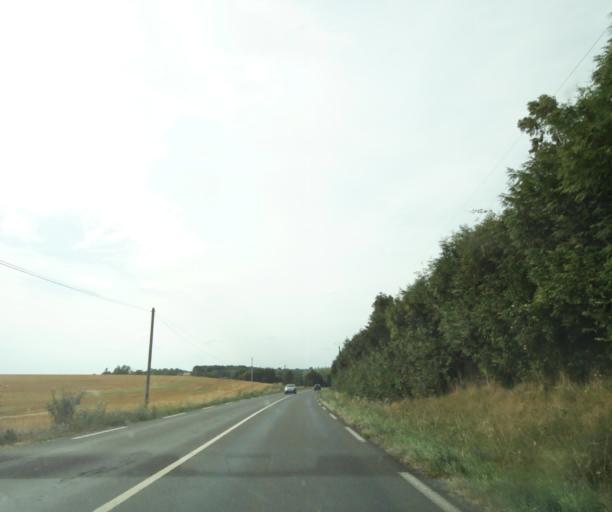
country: FR
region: Centre
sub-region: Departement d'Indre-et-Loire
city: Saint-Christophe-sur-le-Nais
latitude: 47.6569
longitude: 0.4812
